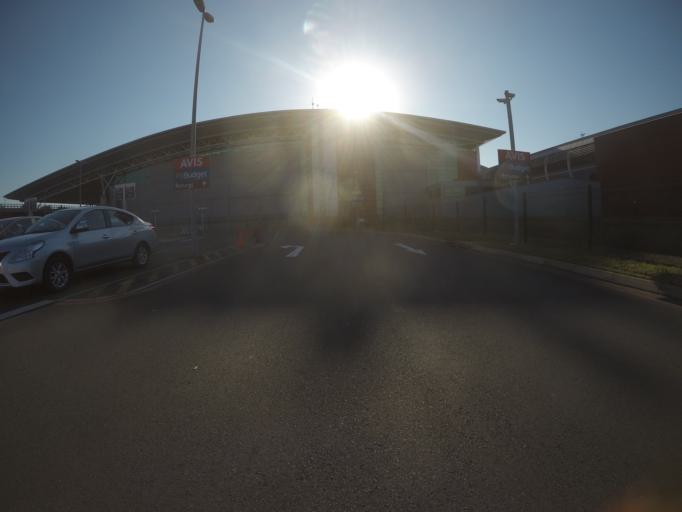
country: ZA
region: KwaZulu-Natal
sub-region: iLembe District Municipality
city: Ballitoville
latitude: -29.6202
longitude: 31.1041
